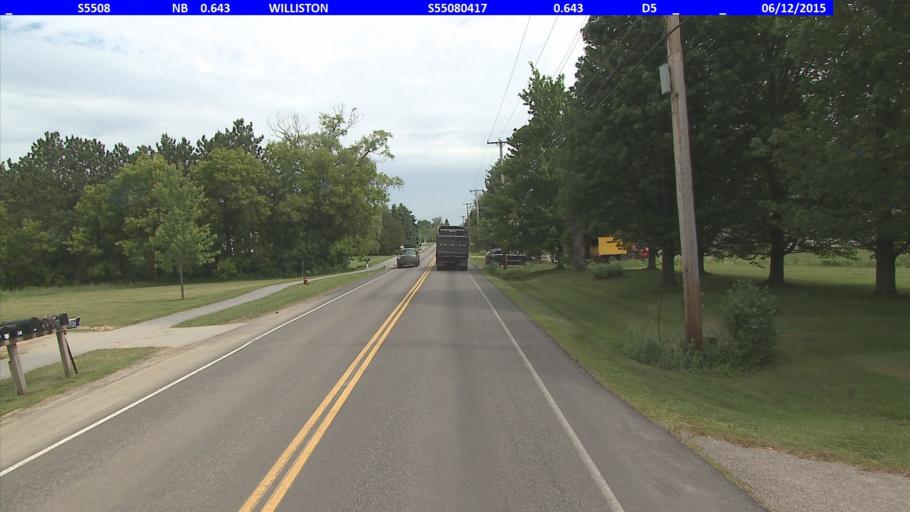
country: US
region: Vermont
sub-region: Chittenden County
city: Williston
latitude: 44.4458
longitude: -73.0628
